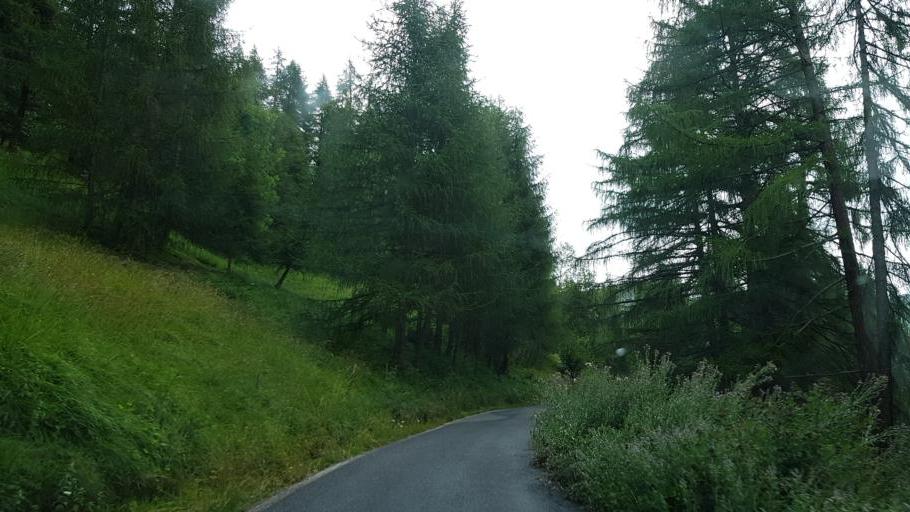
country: IT
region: Piedmont
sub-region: Provincia di Cuneo
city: Stroppo
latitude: 44.5158
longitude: 7.1078
